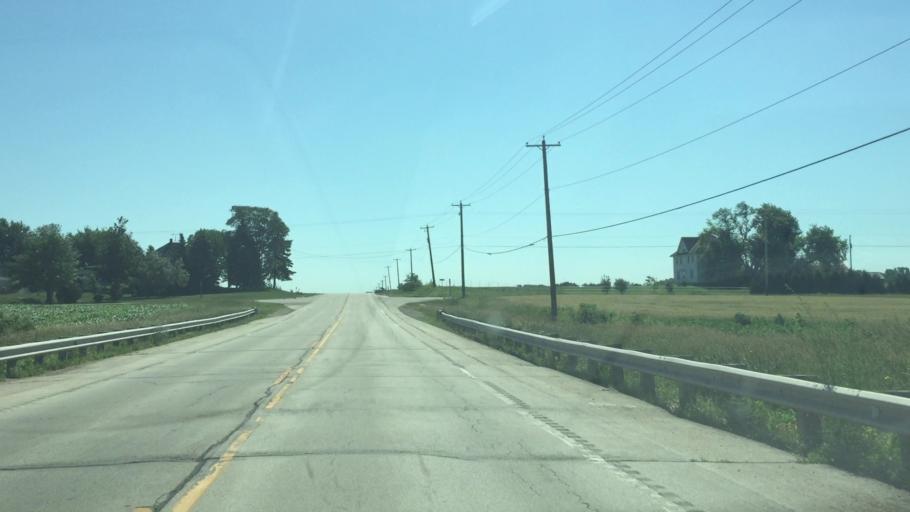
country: US
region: Wisconsin
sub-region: Calumet County
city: Hilbert
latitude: 44.1402
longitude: -88.1858
